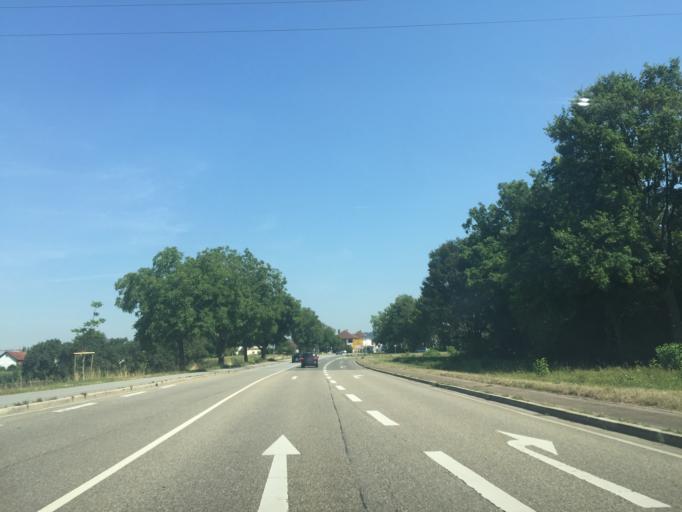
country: DE
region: Baden-Wuerttemberg
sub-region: Karlsruhe Region
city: Weinheim
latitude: 49.5240
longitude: 8.6553
